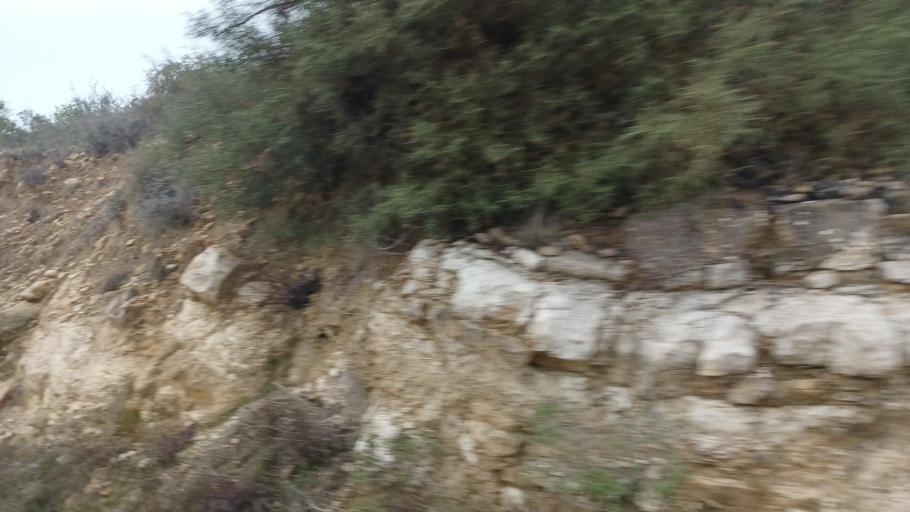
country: CY
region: Limassol
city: Pachna
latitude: 34.7710
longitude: 32.7617
